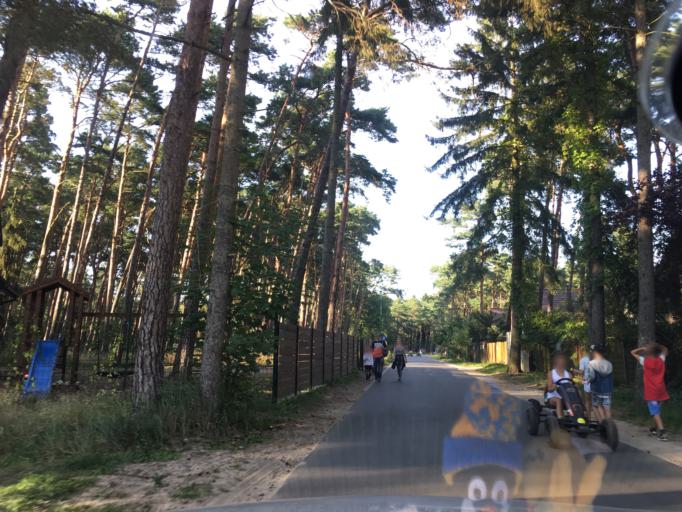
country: PL
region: West Pomeranian Voivodeship
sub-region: Powiat gryficki
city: Pobierowo
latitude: 54.0451
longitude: 14.8742
